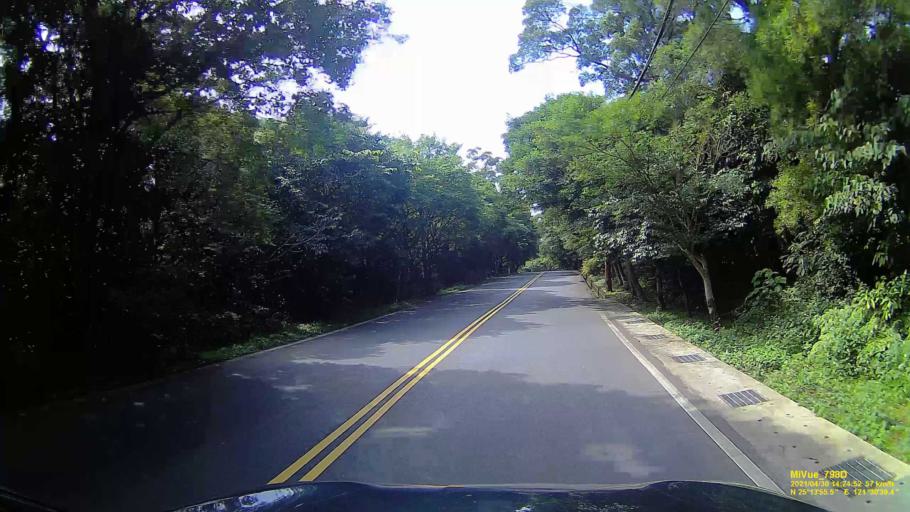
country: TW
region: Taipei
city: Taipei
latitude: 25.2323
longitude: 121.5107
